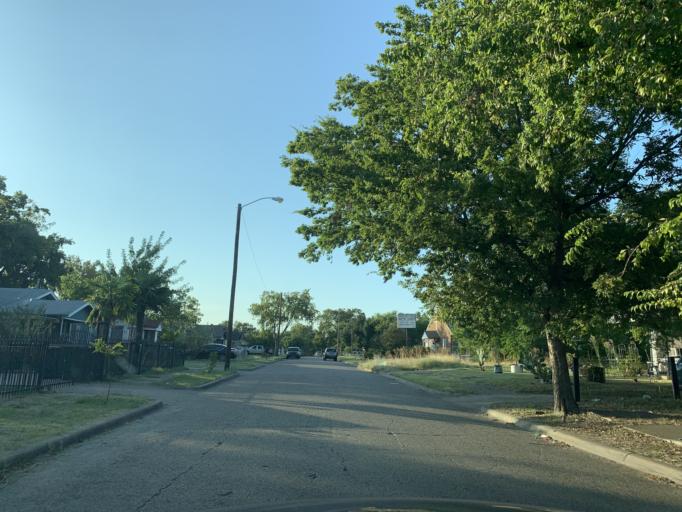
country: US
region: Texas
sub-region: Dallas County
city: Dallas
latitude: 32.7097
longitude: -96.8044
